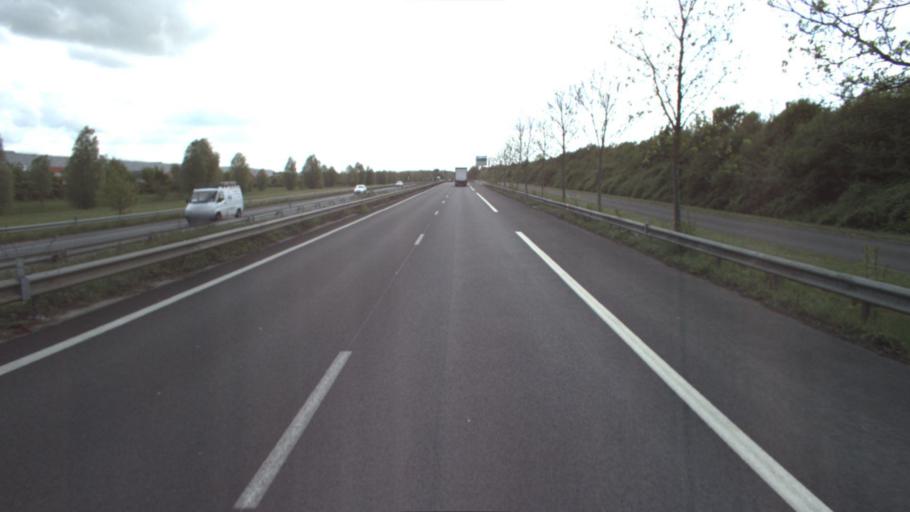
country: FR
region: Ile-de-France
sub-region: Departement de Seine-et-Marne
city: Fontenay-Tresigny
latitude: 48.7233
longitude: 2.8314
